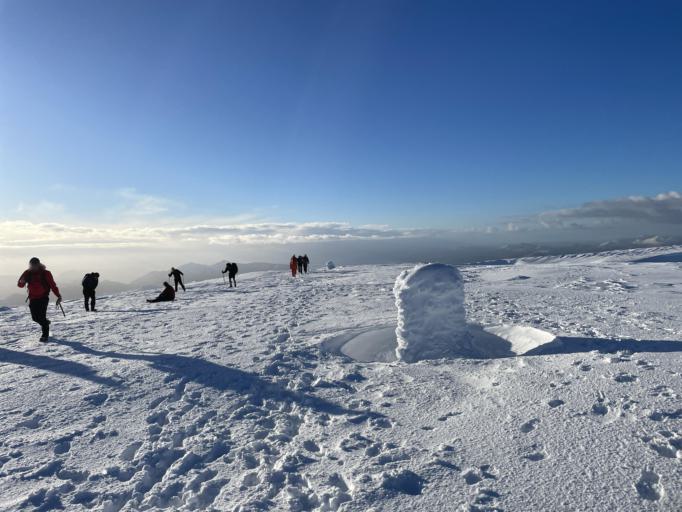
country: GB
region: Scotland
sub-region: Highland
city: Fort William
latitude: 56.7966
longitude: -5.0040
